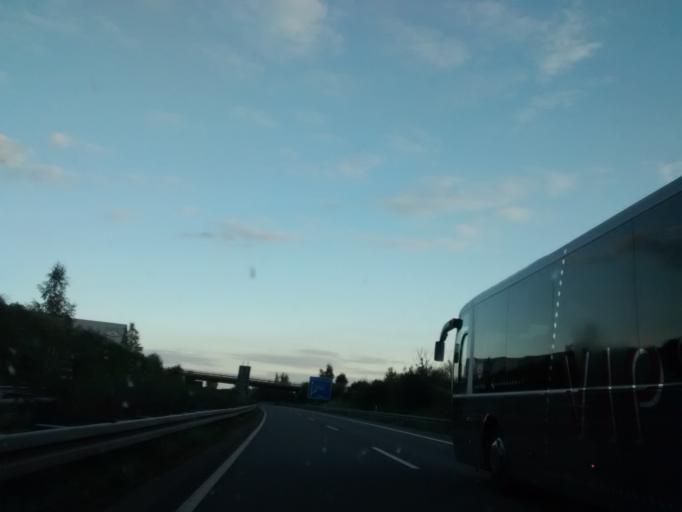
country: DE
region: Lower Saxony
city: Dissen
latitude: 52.1076
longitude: 8.1846
